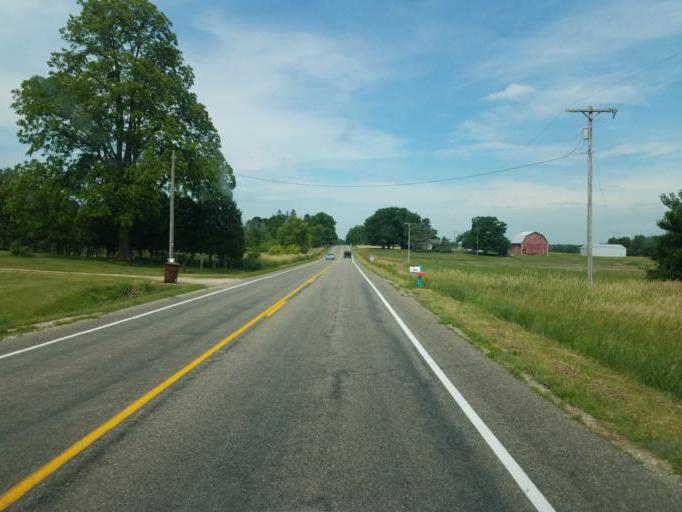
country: US
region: Michigan
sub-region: Eaton County
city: Charlotte
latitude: 42.6261
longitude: -84.8705
